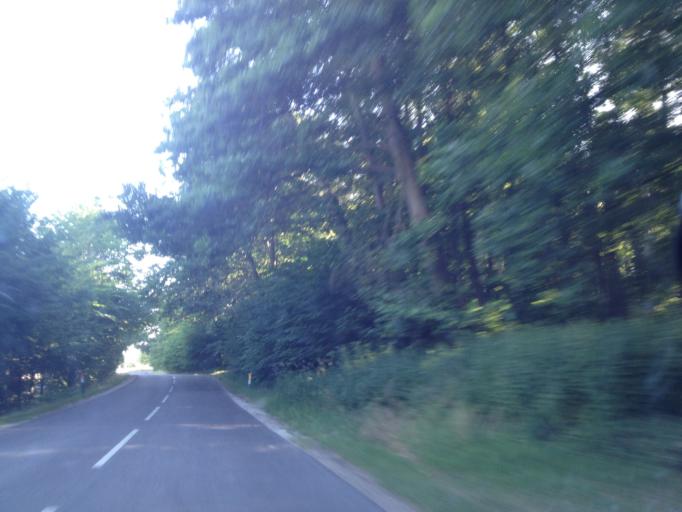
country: DK
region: Capital Region
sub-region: Gribskov Kommune
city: Helsinge
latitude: 56.0402
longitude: 12.1077
